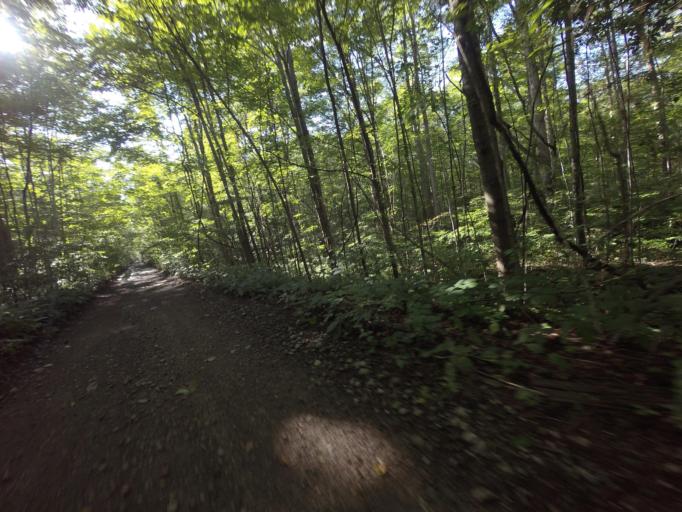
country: CA
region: Ontario
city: Goderich
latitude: 43.7538
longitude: -81.5658
